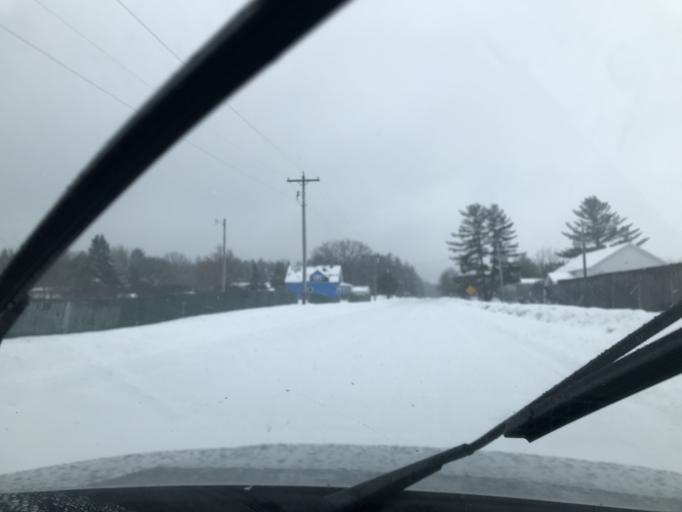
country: US
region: Wisconsin
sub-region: Marinette County
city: Peshtigo
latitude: 45.3791
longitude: -87.9470
